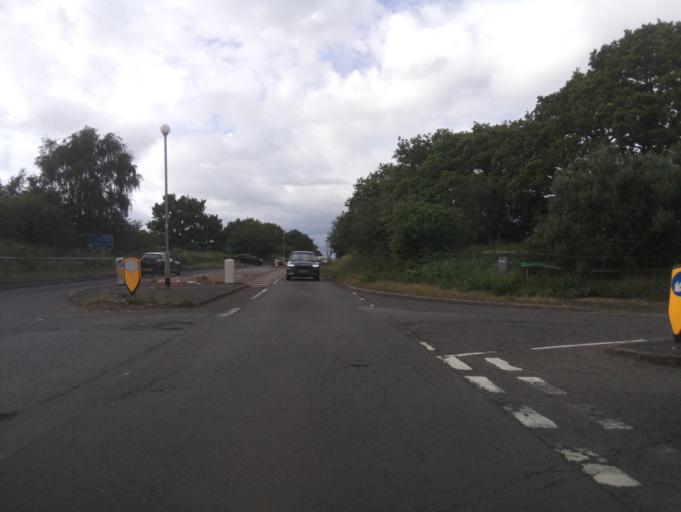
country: GB
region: England
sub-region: Dudley
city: Kingswinford
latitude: 52.4885
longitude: -2.1898
